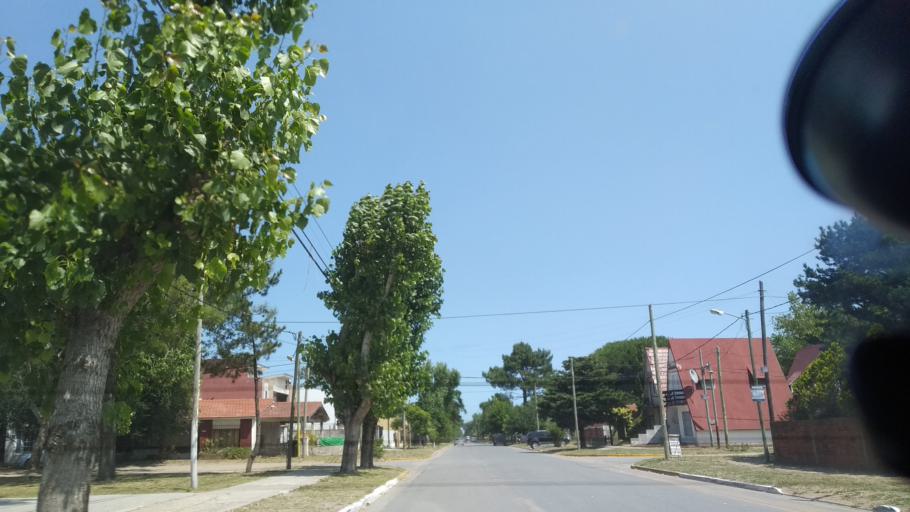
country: AR
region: Buenos Aires
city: Mar del Tuyu
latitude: -36.5707
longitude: -56.6940
